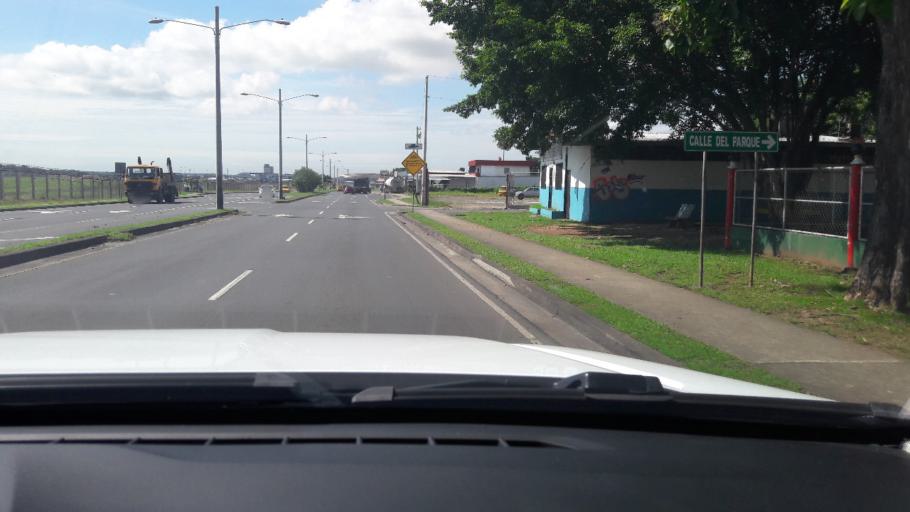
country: PA
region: Panama
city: Tocumen
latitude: 9.0832
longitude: -79.3846
